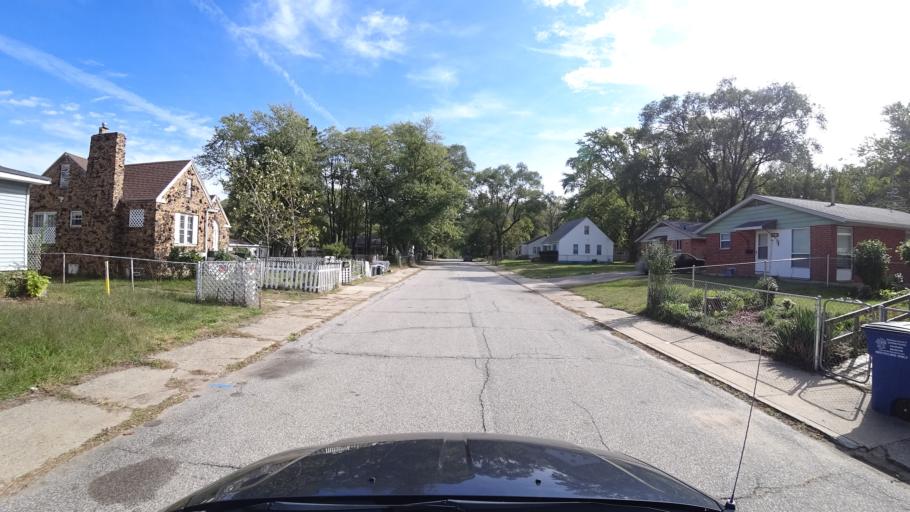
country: US
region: Indiana
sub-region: LaPorte County
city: Michigan City
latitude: 41.7198
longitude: -86.8889
